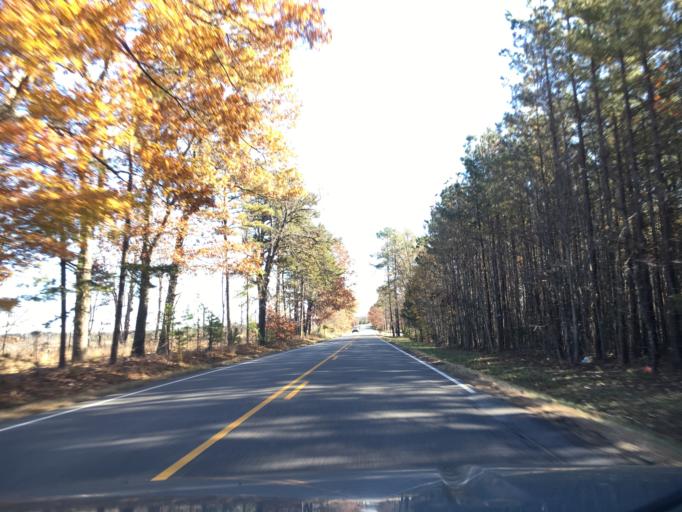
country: US
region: Virginia
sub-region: Appomattox County
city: Appomattox
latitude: 37.4563
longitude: -78.6959
